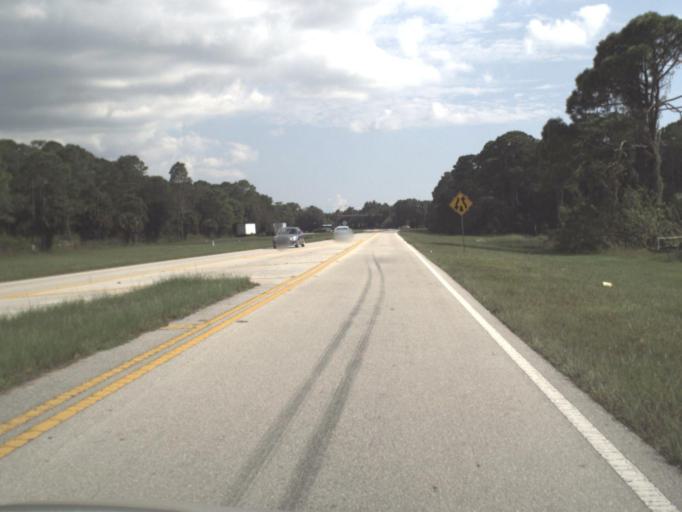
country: US
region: Florida
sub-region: Sarasota County
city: Plantation
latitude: 27.1029
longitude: -82.3454
